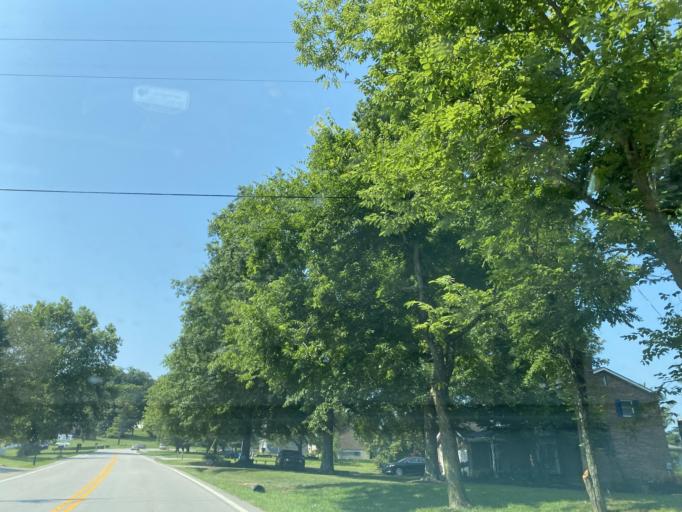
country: US
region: Kentucky
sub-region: Kenton County
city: Ryland Heights
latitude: 38.9244
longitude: -84.4398
